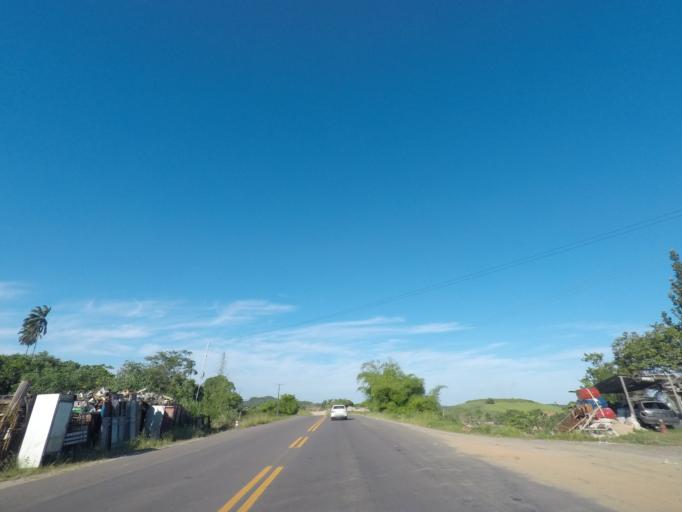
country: BR
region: Bahia
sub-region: Nazare
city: Nazare
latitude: -13.0250
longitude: -38.9886
